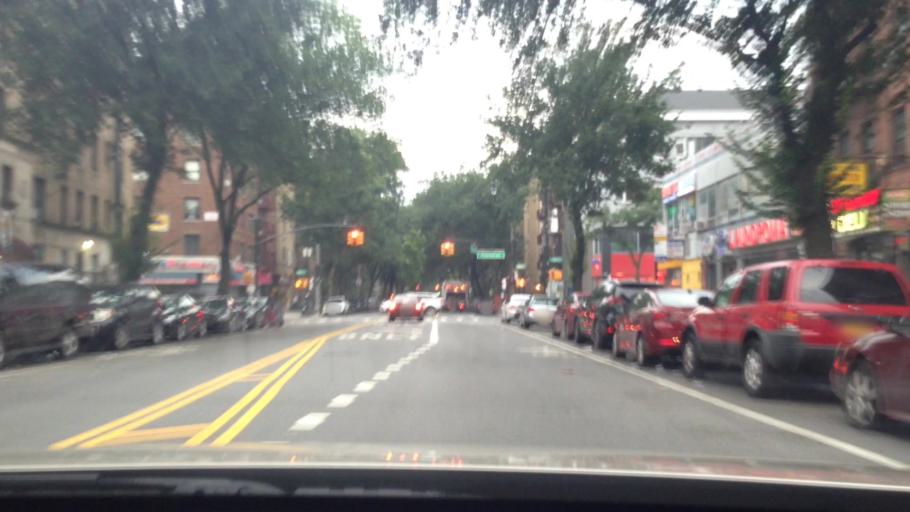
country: US
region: New York
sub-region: Kings County
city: Brooklyn
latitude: 40.6494
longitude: -73.9609
